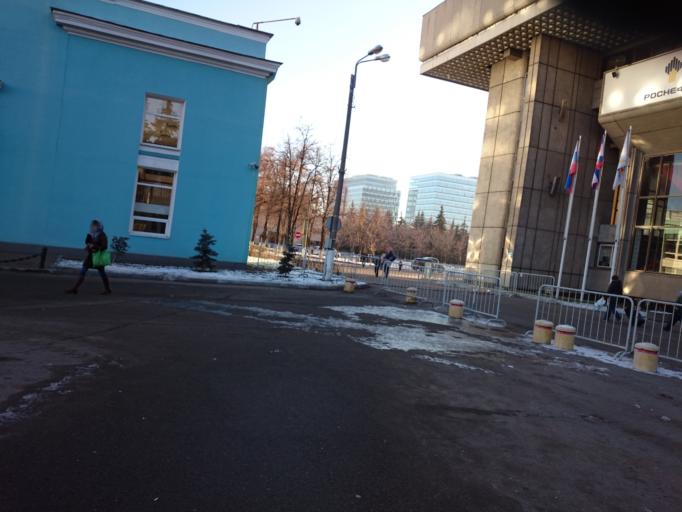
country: RU
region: Moscow
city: Sokol
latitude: 55.7954
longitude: 37.5392
